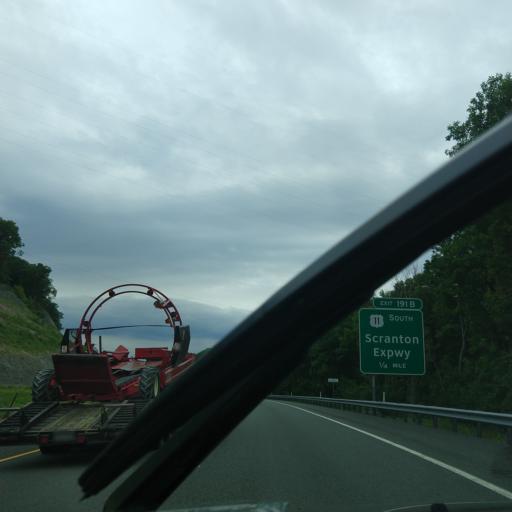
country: US
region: Pennsylvania
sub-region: Lackawanna County
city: Chinchilla
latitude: 41.4628
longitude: -75.6670
